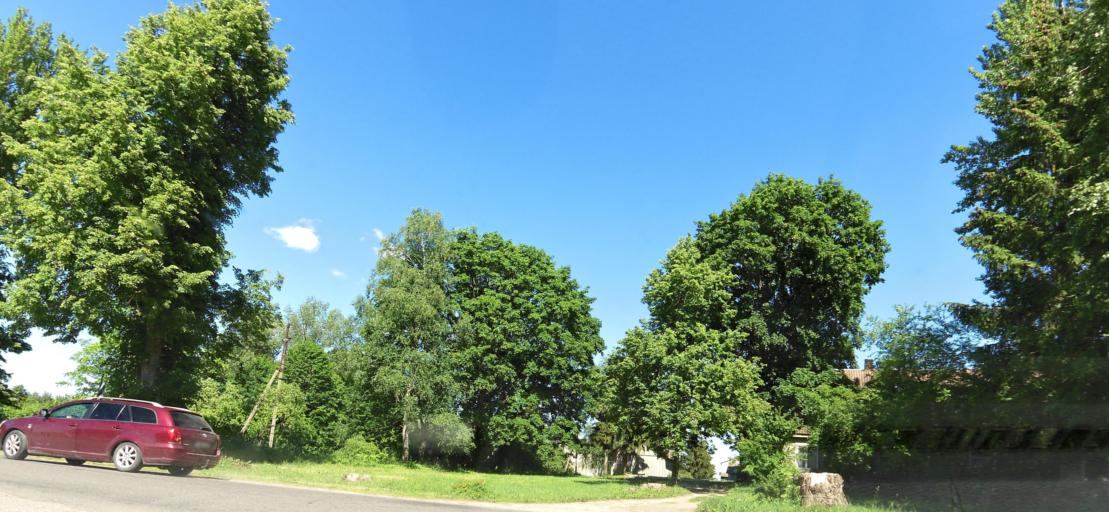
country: LT
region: Utenos apskritis
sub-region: Anyksciai
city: Anyksciai
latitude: 55.3486
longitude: 25.1205
